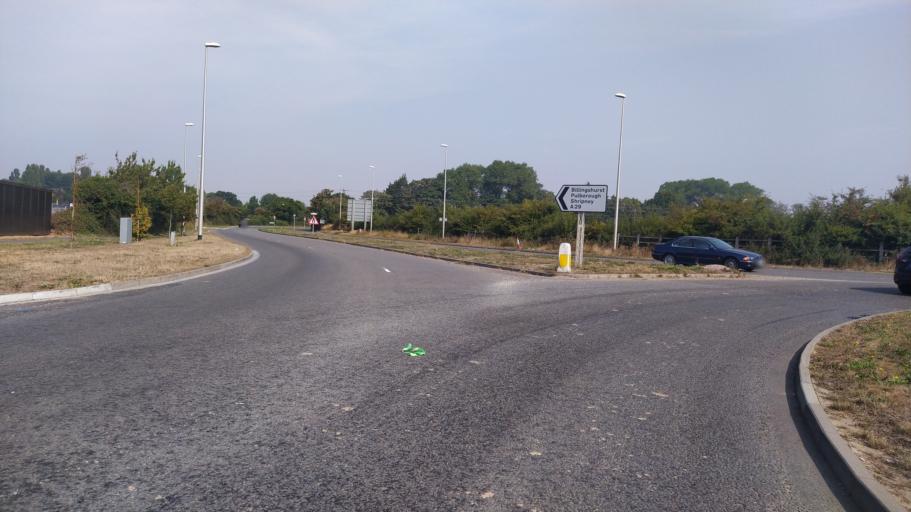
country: GB
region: England
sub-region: West Sussex
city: Bognor Regis
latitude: 50.8066
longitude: -0.6672
